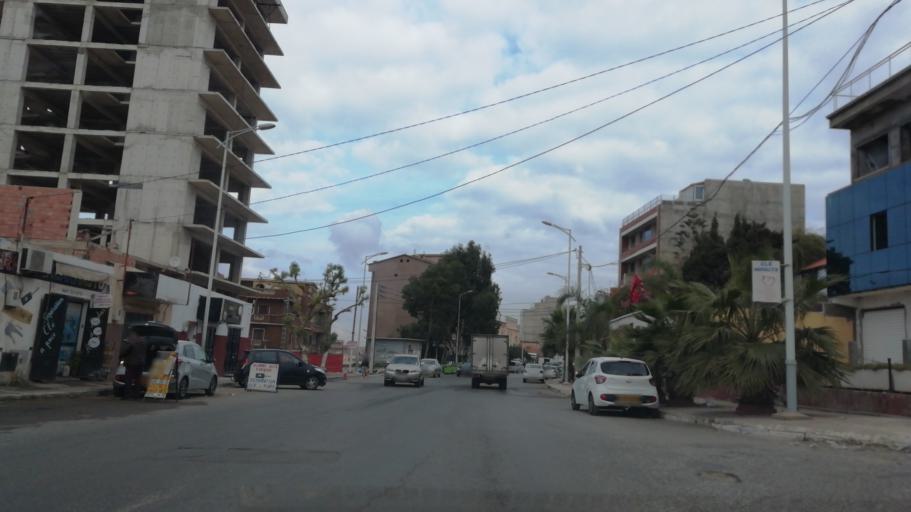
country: DZ
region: Oran
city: Oran
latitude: 35.7078
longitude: -0.6110
